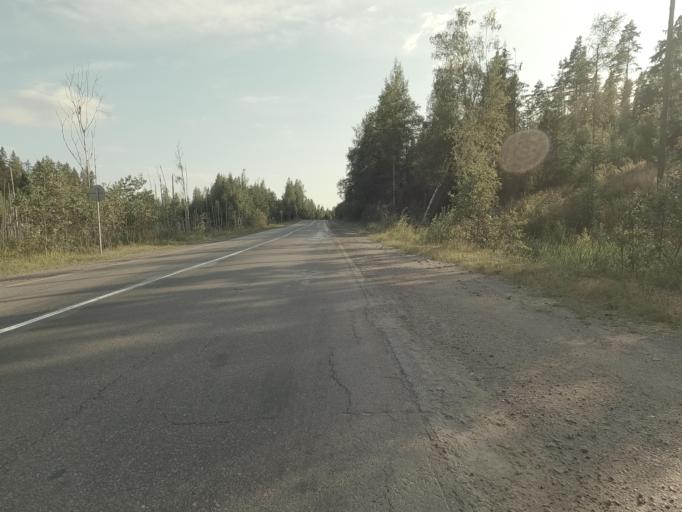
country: RU
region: Leningrad
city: Vyborg
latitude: 60.8486
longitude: 28.8611
